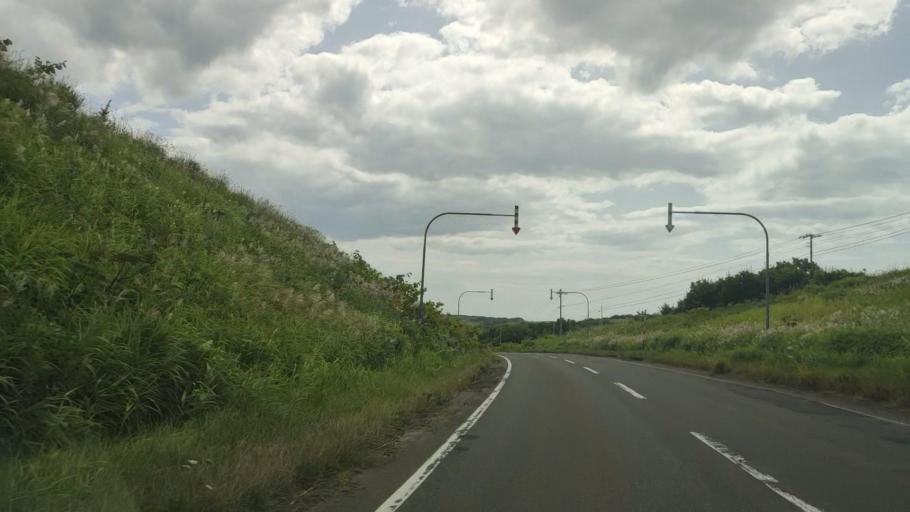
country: JP
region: Hokkaido
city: Rumoi
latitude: 44.6005
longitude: 141.7916
